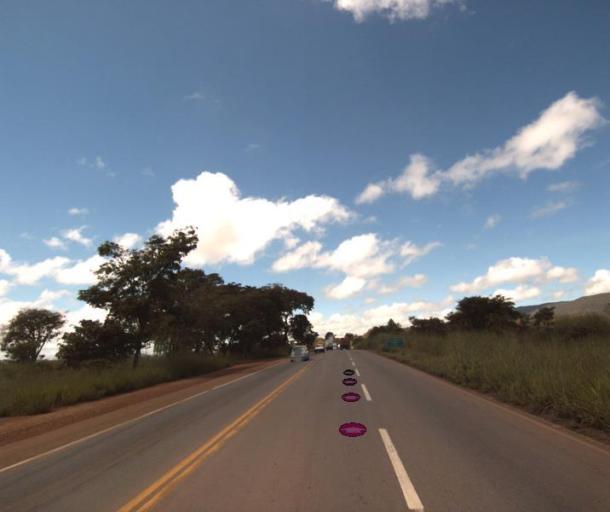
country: BR
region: Goias
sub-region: Jaragua
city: Jaragua
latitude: -15.7720
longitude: -49.3078
